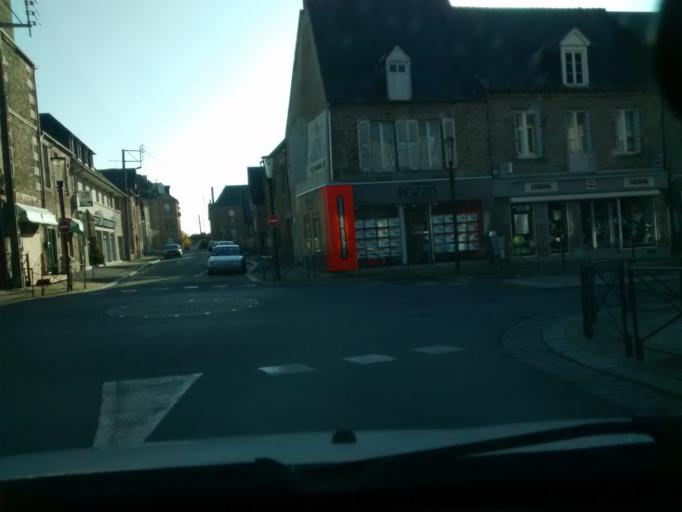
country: FR
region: Lower Normandy
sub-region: Departement de la Manche
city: Pontorson
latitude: 48.5532
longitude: -1.5093
